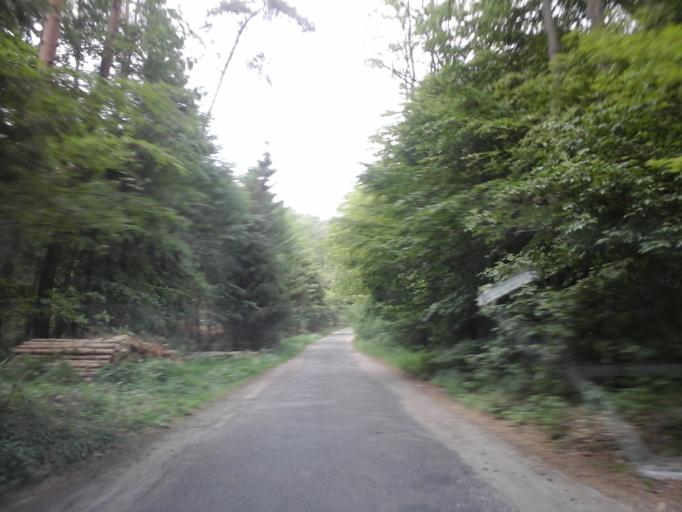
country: PL
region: West Pomeranian Voivodeship
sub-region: Powiat mysliborski
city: Barlinek
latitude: 53.0204
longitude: 15.2224
